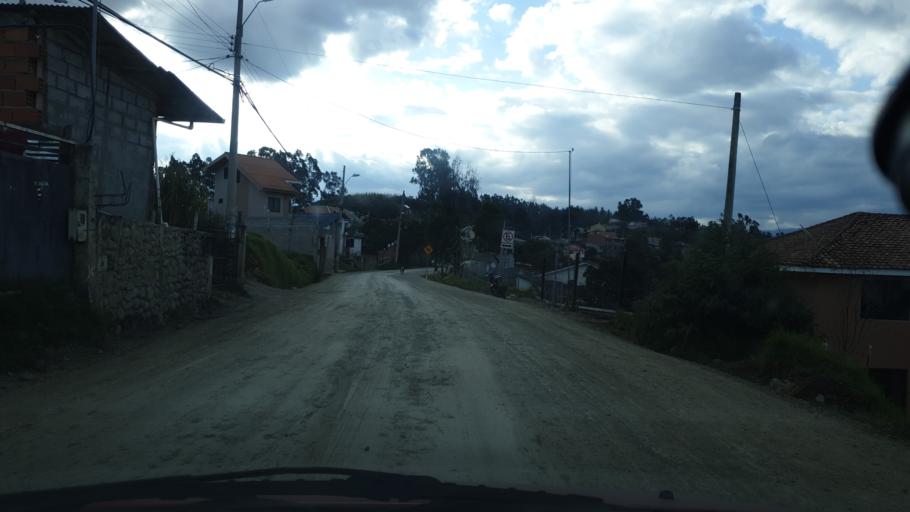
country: EC
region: Azuay
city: Cuenca
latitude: -2.9233
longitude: -78.9738
